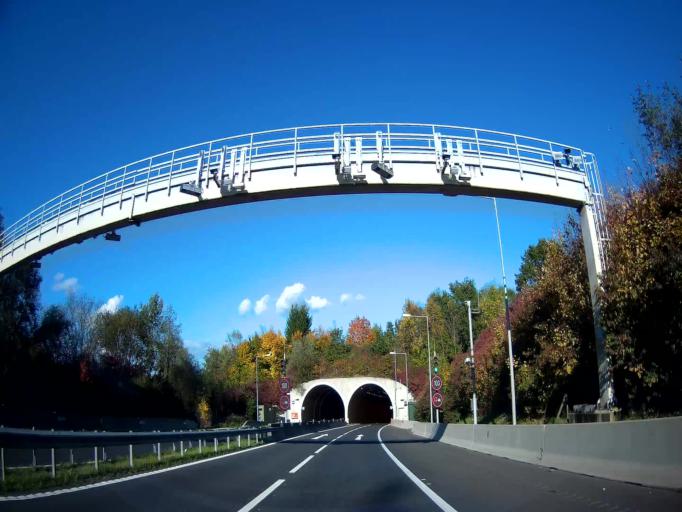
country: AT
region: Carinthia
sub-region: Klagenfurt am Woerthersee
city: Klagenfurt am Woerthersee
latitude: 46.6478
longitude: 14.2534
